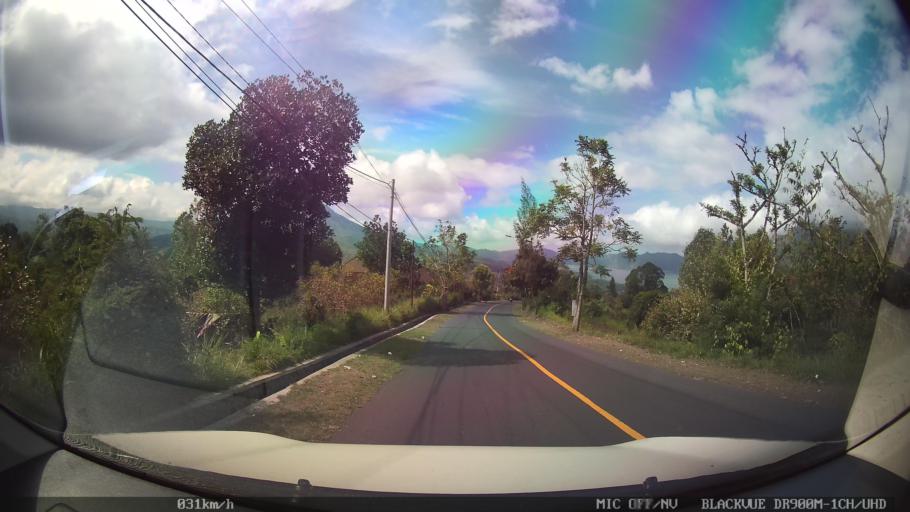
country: ID
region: Bali
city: Banjar Kedisan
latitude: -8.2813
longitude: 115.3664
